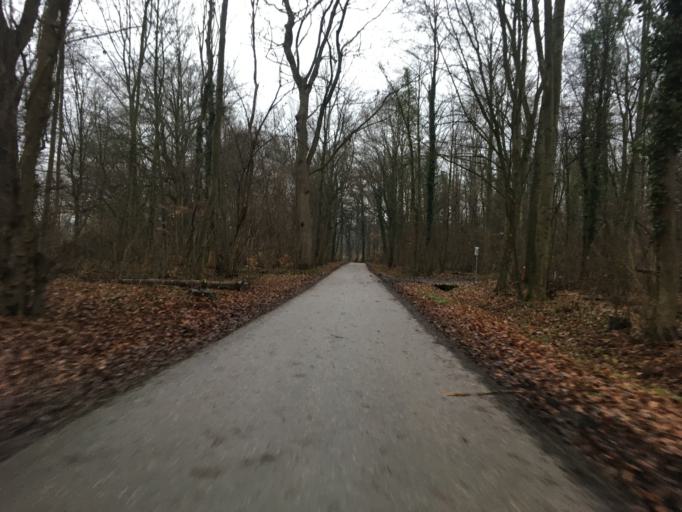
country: DE
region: Baden-Wuerttemberg
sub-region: Karlsruhe Region
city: Ettlingen
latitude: 48.9605
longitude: 8.4308
